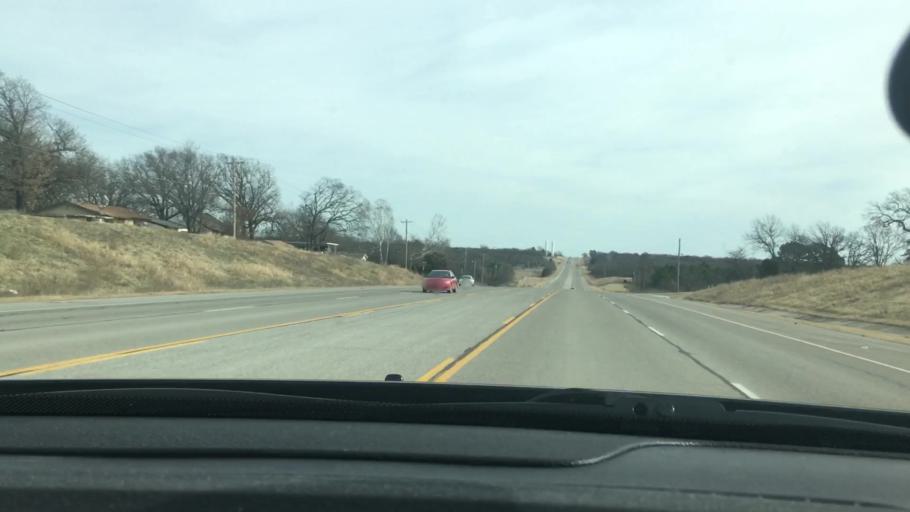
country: US
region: Oklahoma
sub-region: Carter County
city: Dickson
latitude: 34.1871
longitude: -97.0184
